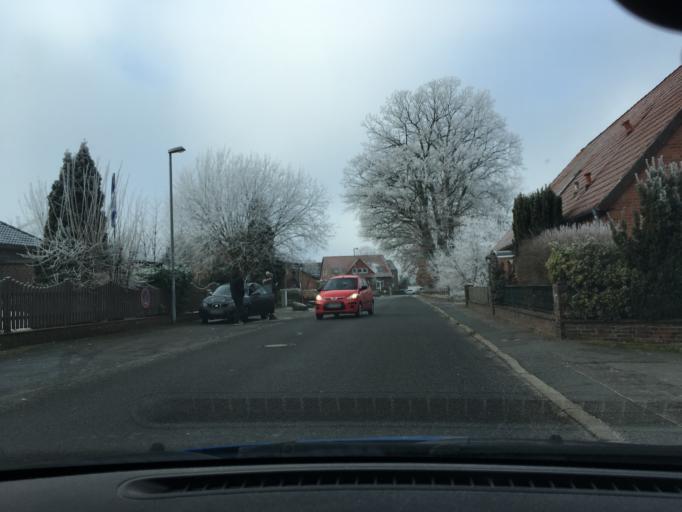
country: DE
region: Lower Saxony
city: Bardowick
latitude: 53.2746
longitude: 10.3911
